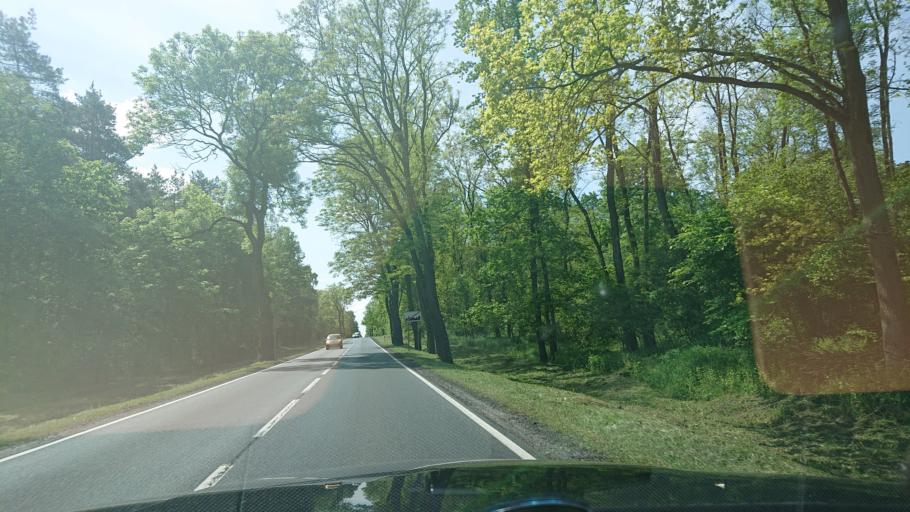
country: PL
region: Greater Poland Voivodeship
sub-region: Powiat gnieznienski
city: Gniezno
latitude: 52.4919
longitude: 17.5939
